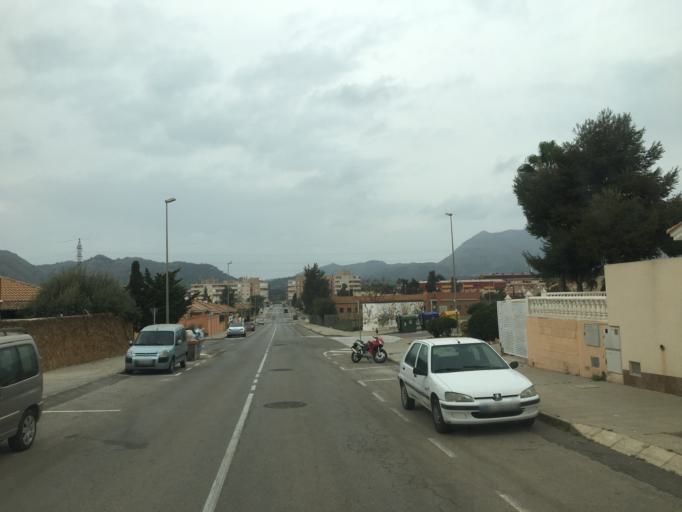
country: ES
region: Murcia
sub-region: Murcia
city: Cartagena
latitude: 37.6198
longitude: -1.0210
